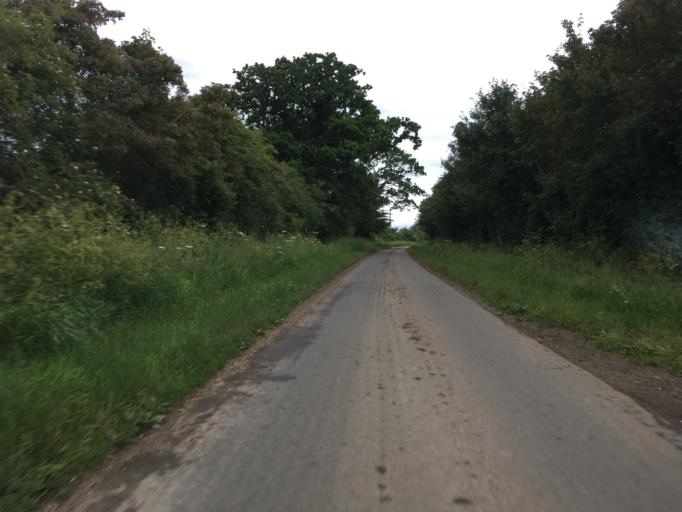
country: GB
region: England
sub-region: Wiltshire
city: Norton
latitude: 51.5988
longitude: -2.1712
